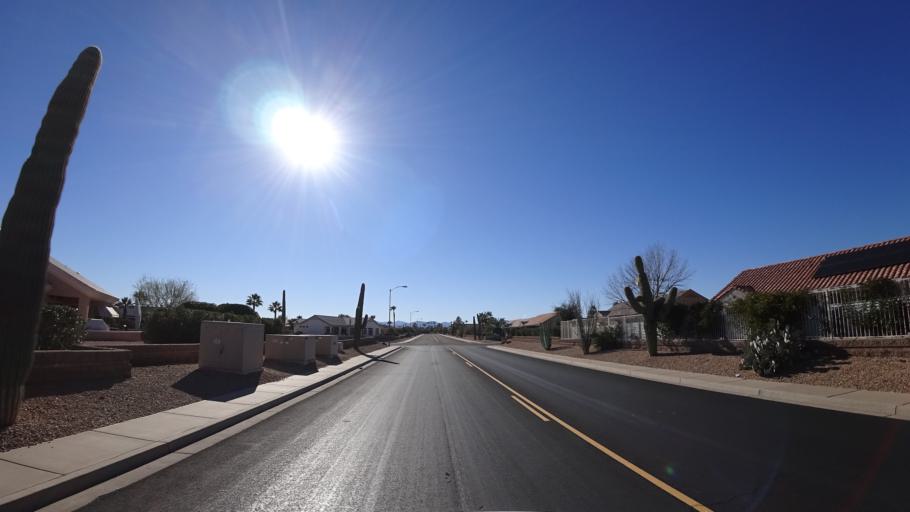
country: US
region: Arizona
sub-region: Maricopa County
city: Sun City West
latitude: 33.6929
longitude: -112.3773
